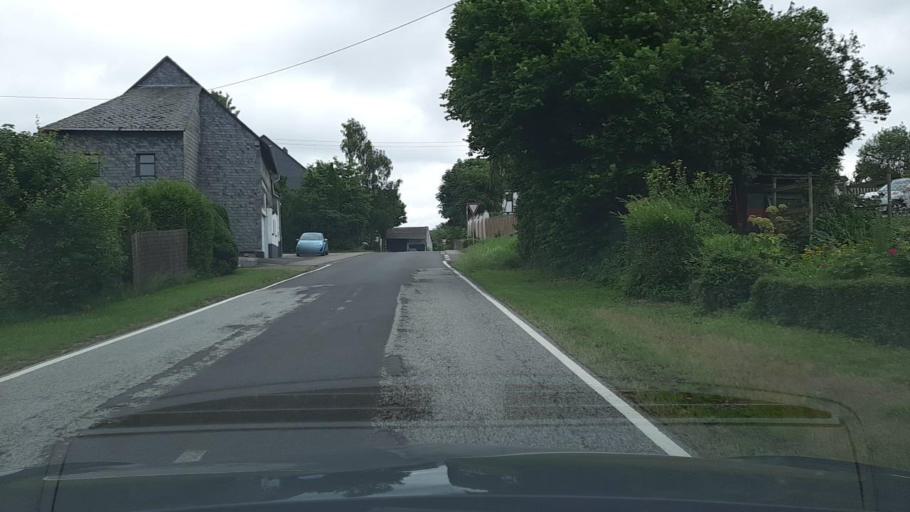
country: DE
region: Rheinland-Pfalz
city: Roth
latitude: 50.0883
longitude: 7.4542
